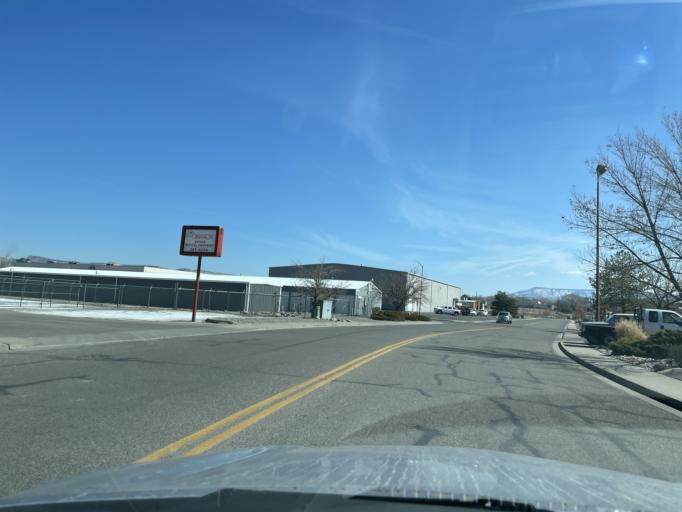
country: US
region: Colorado
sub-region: Mesa County
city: Grand Junction
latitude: 39.0729
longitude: -108.5782
